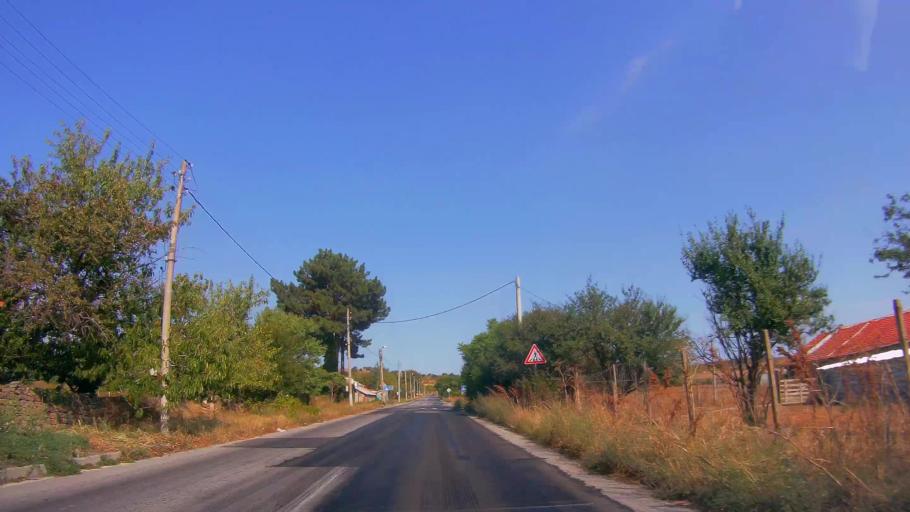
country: BG
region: Burgas
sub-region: Obshtina Karnobat
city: Karnobat
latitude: 42.7270
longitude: 26.8969
